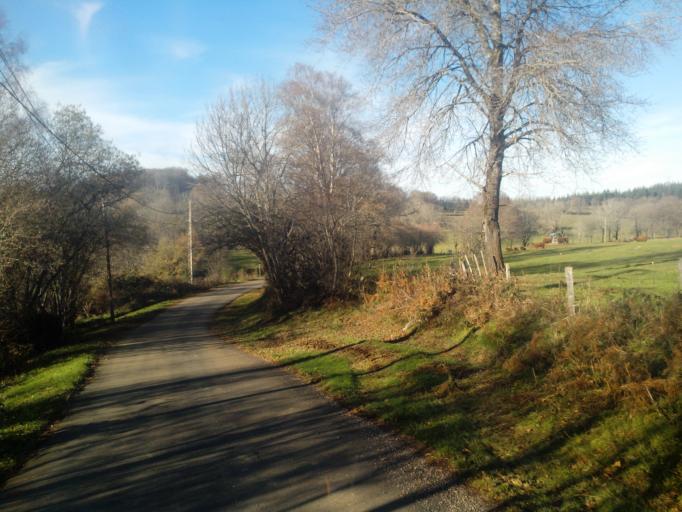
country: FR
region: Limousin
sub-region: Departement de la Correze
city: Bort-les-Orgues
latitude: 45.3970
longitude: 2.4786
